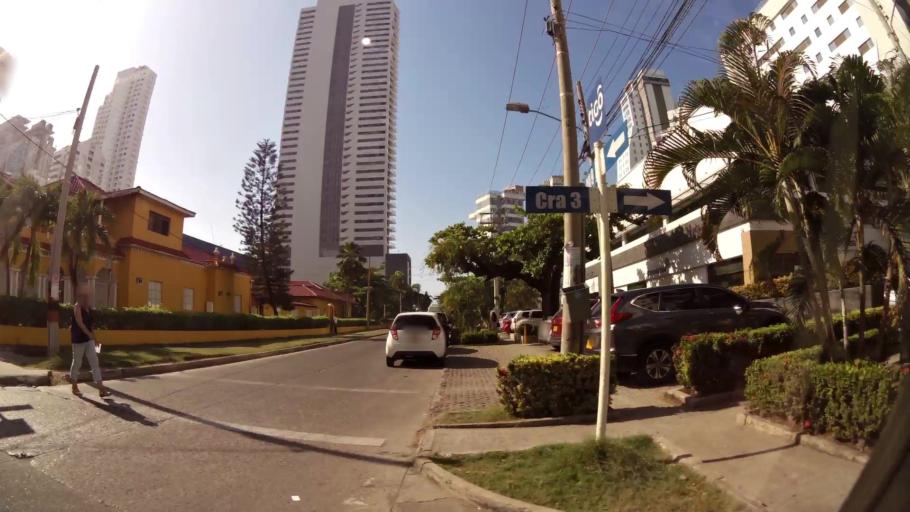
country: CO
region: Bolivar
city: Cartagena
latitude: 10.4046
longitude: -75.5527
